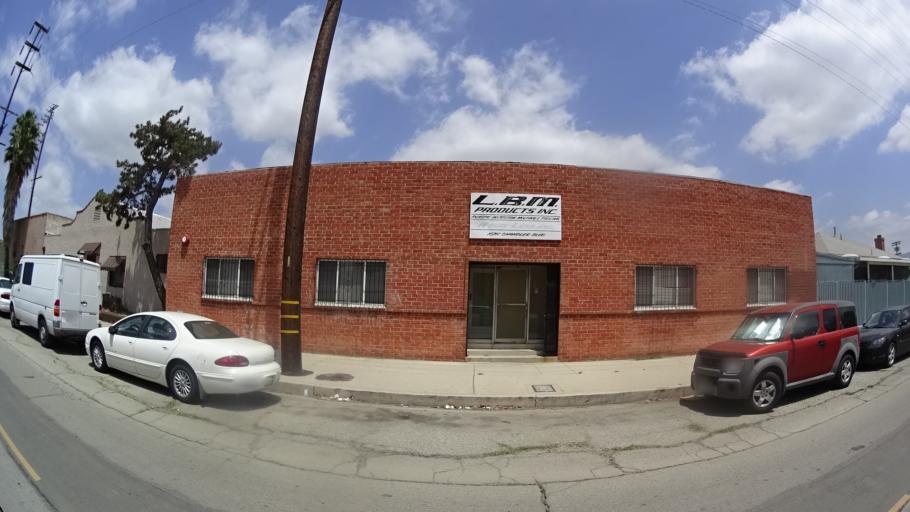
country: US
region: California
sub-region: Los Angeles County
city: North Hollywood
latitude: 34.1686
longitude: -118.3643
